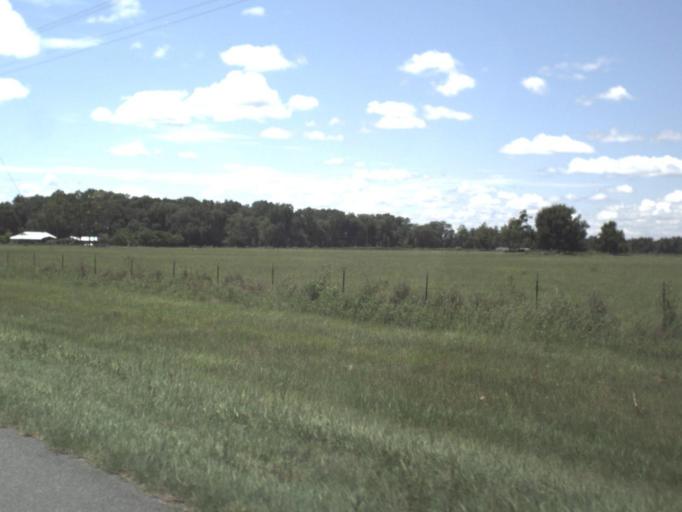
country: US
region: Florida
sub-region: Lafayette County
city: Mayo
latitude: 30.1257
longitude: -83.2725
